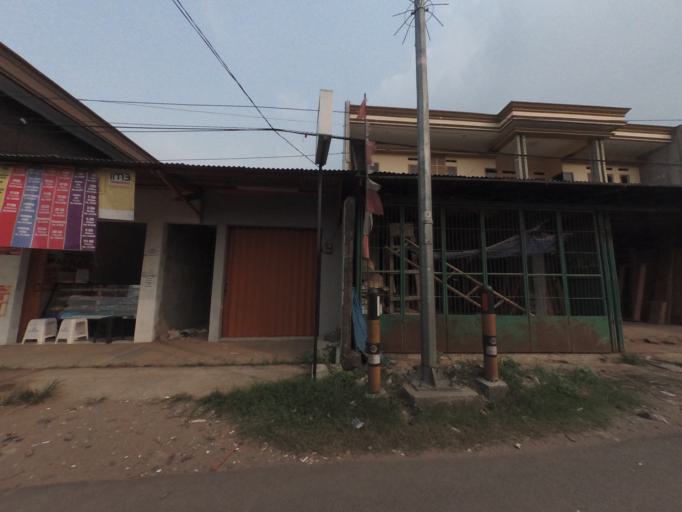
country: ID
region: West Java
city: Ciampea
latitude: -6.5710
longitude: 106.6677
